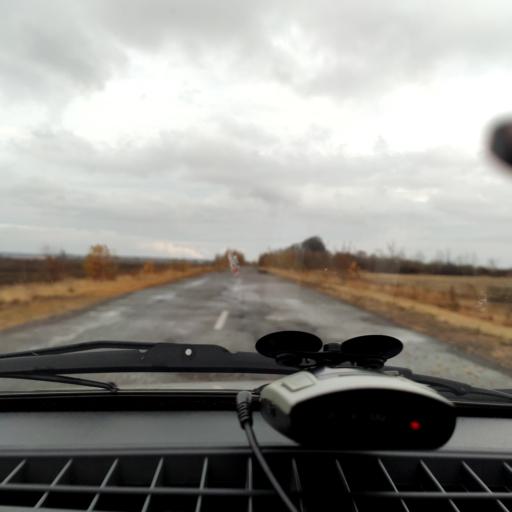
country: RU
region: Voronezj
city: Kolodeznyy
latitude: 51.2431
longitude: 38.9949
